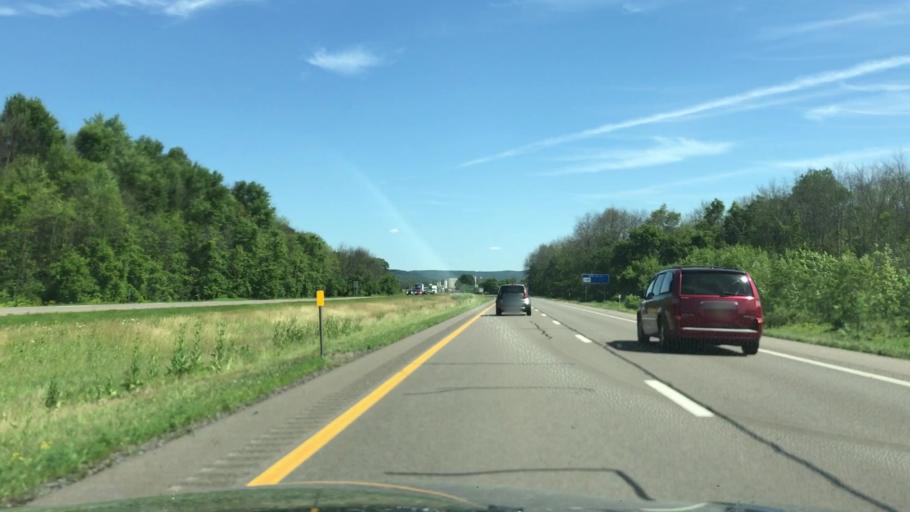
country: US
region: New York
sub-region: Steuben County
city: Gang Mills
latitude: 42.2370
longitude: -77.1935
